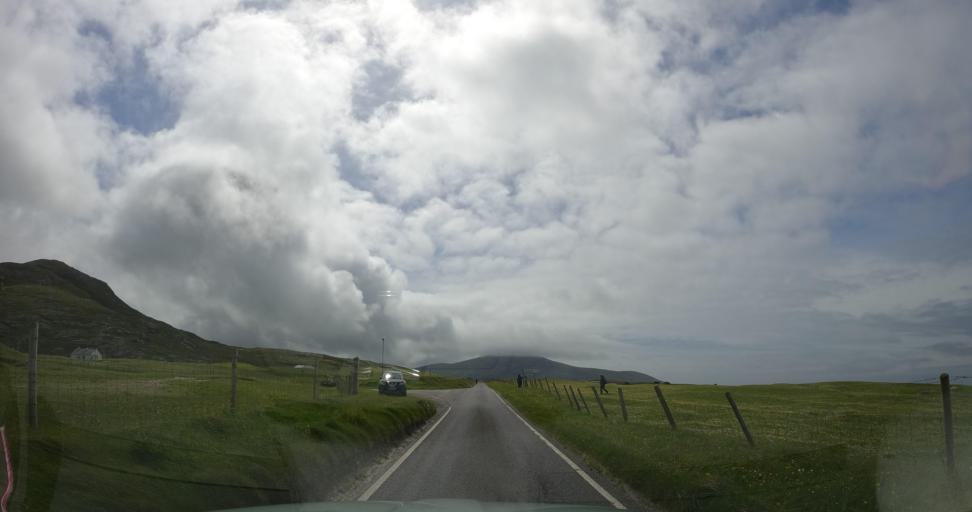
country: GB
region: Scotland
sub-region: Eilean Siar
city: Barra
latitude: 56.9974
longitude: -7.5060
